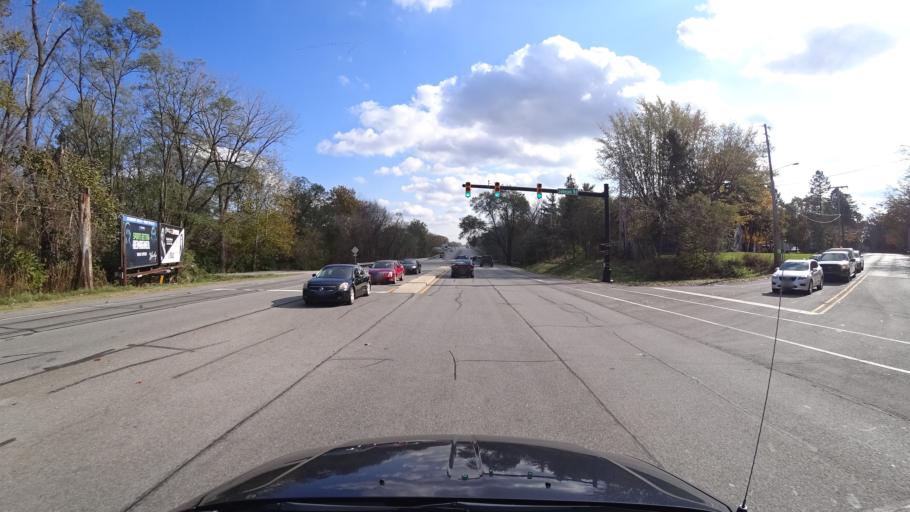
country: US
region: Indiana
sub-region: LaPorte County
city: Trail Creek
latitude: 41.7058
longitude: -86.8581
